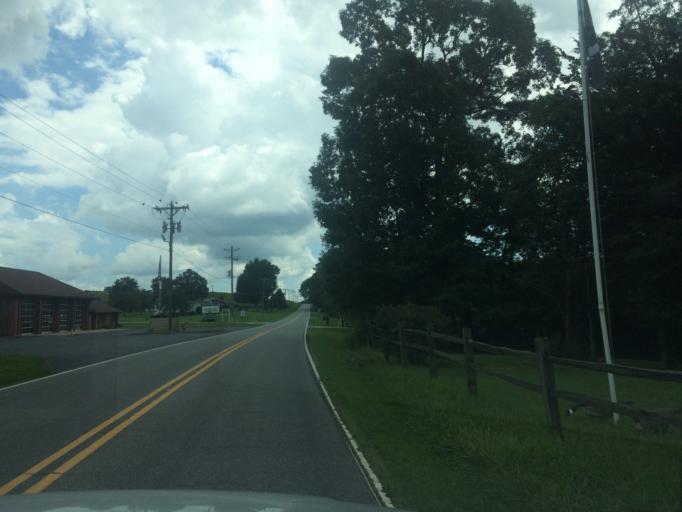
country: US
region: South Carolina
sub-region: Spartanburg County
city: Landrum
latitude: 35.2262
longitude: -82.0575
